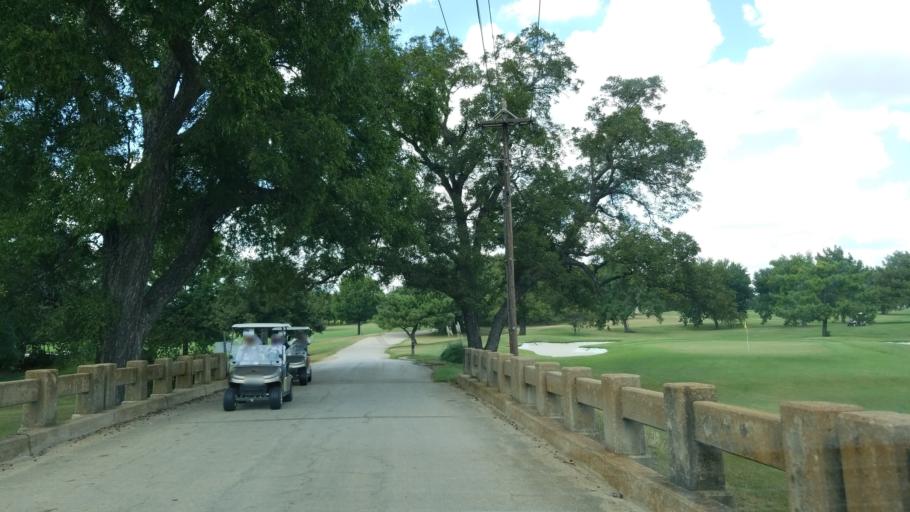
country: US
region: Texas
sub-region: Tarrant County
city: Euless
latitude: 32.8596
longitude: -97.0603
